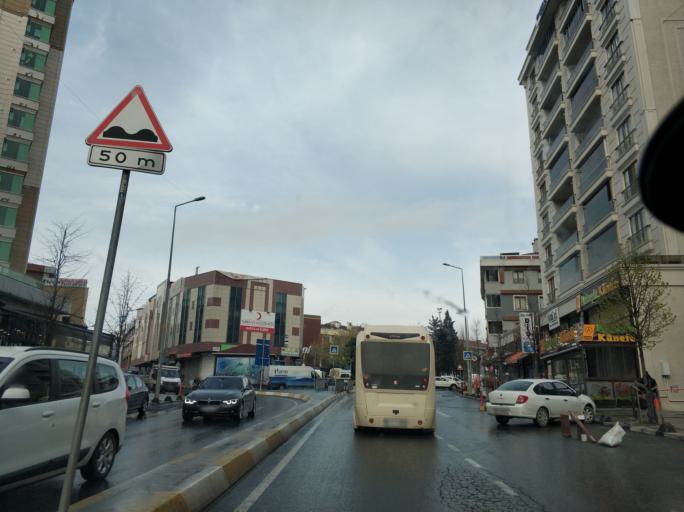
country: TR
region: Istanbul
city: Mahmutbey
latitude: 41.0310
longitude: 28.8300
